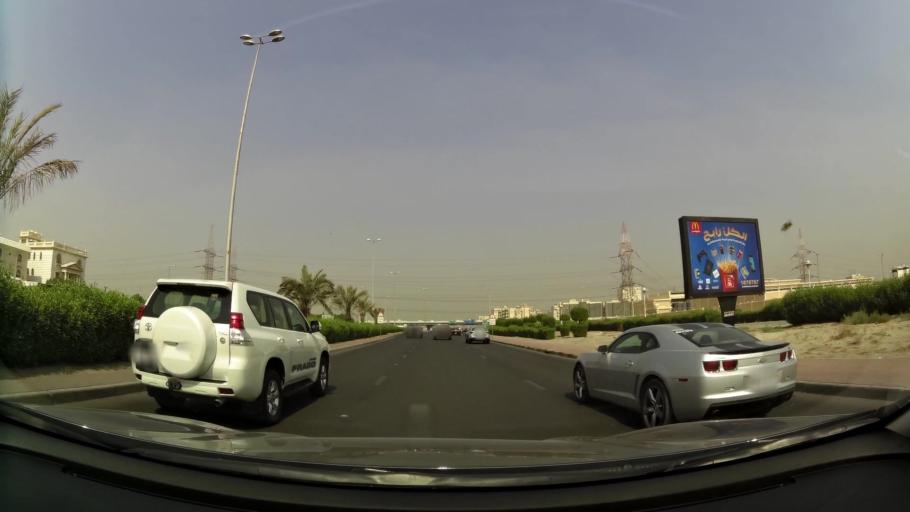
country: KW
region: Al Asimah
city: Ar Rabiyah
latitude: 29.2956
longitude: 47.9058
